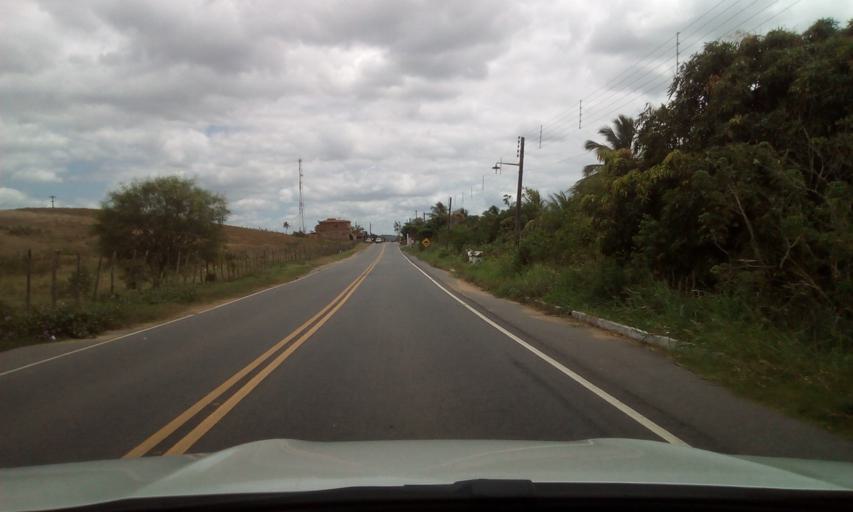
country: BR
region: Paraiba
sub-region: Serra Redonda
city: Alagoa Grande
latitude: -7.1868
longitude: -35.5884
